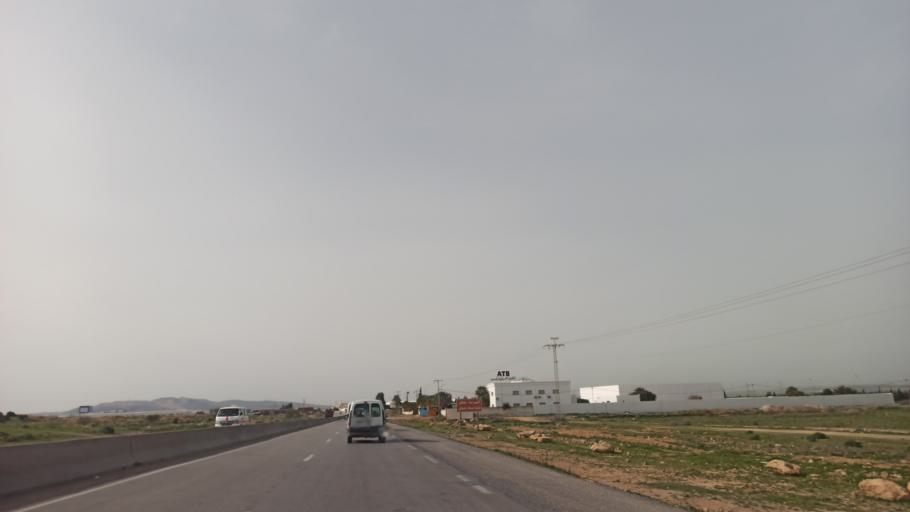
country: TN
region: Tunis
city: La Mohammedia
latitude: 36.5894
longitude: 10.1047
